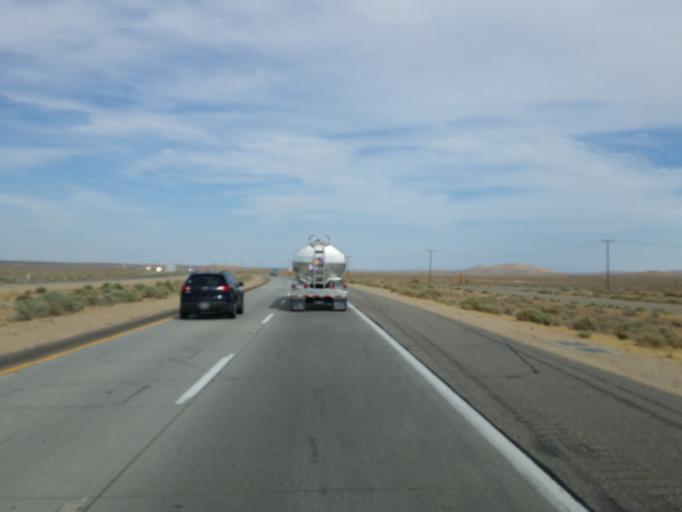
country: US
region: California
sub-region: Kern County
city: Mojave
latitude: 35.0318
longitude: -118.0980
